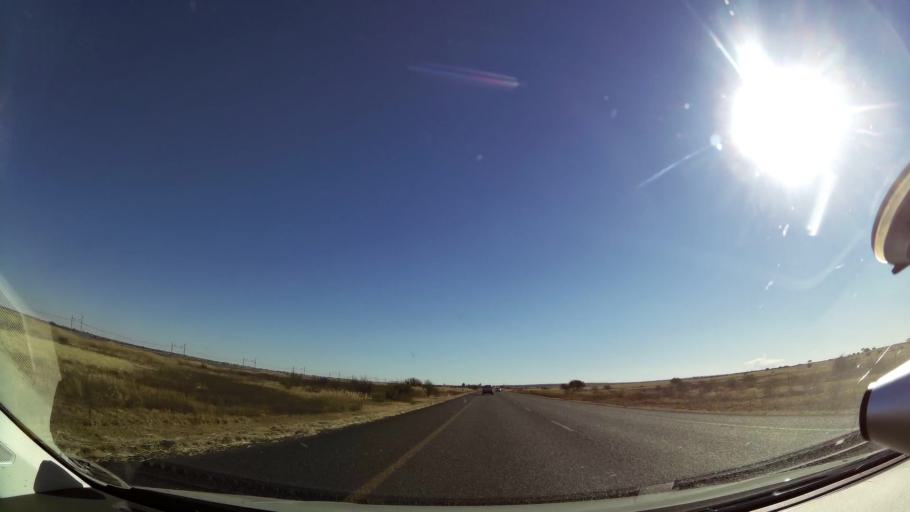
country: ZA
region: Northern Cape
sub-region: Frances Baard District Municipality
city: Kimberley
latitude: -28.6796
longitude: 24.7778
